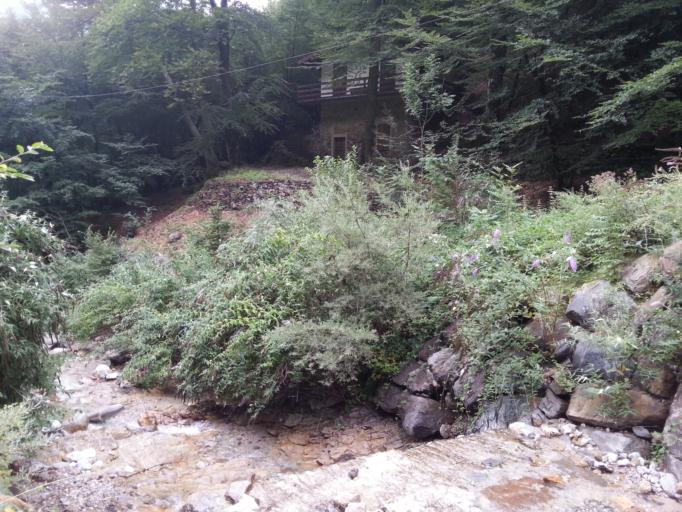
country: IT
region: Lombardy
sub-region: Provincia di Lecco
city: Cortenova
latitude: 45.9915
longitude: 9.3839
